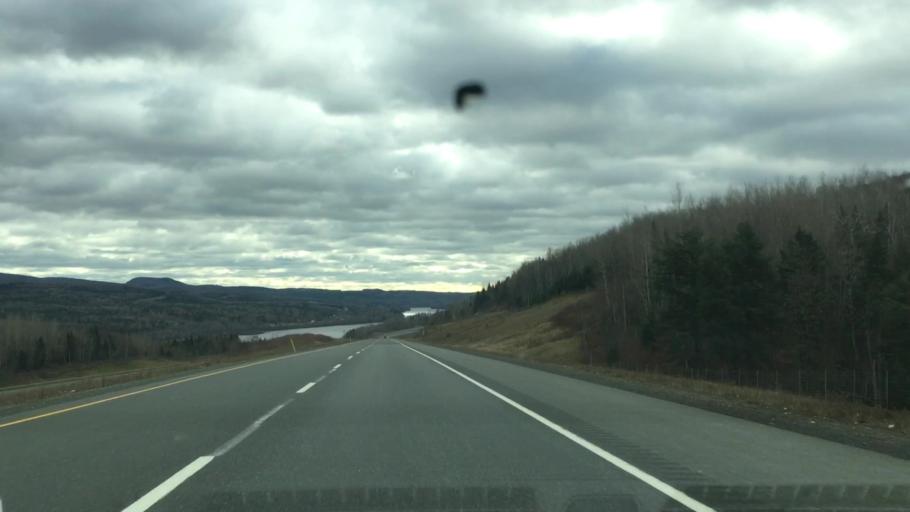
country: US
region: Maine
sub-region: Aroostook County
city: Fort Fairfield
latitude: 46.6898
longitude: -67.7379
